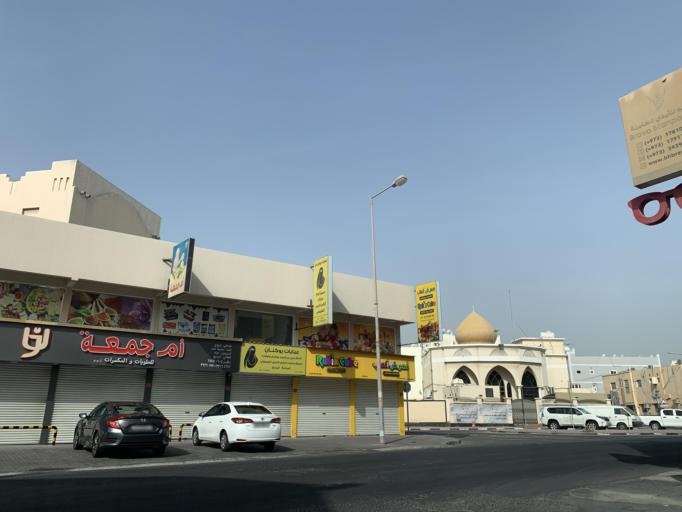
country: BH
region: Northern
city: Madinat `Isa
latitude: 26.1798
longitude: 50.5613
